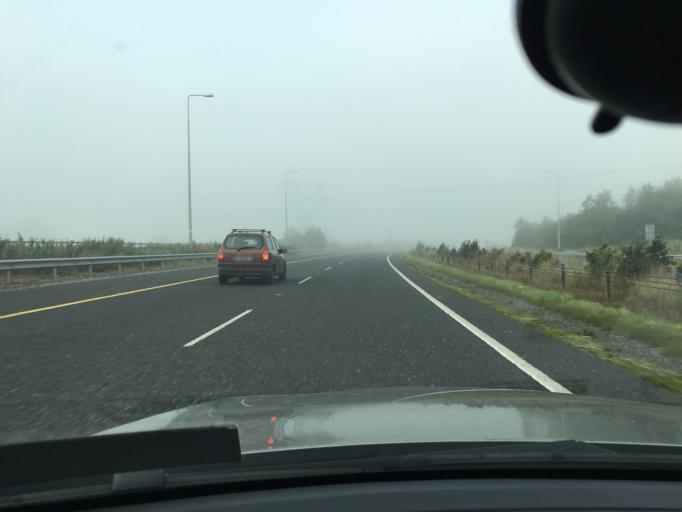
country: IE
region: Leinster
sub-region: An Mhi
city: Enfield
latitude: 53.4113
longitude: -6.8865
